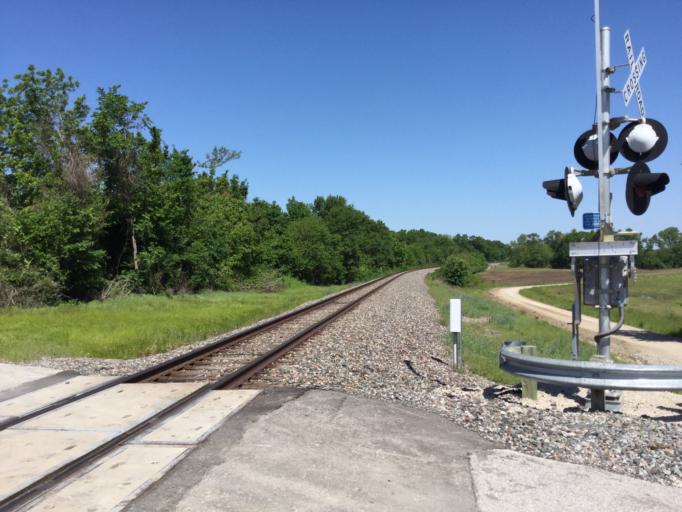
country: US
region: Kansas
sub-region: Labette County
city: Parsons
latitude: 37.2742
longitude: -95.2302
